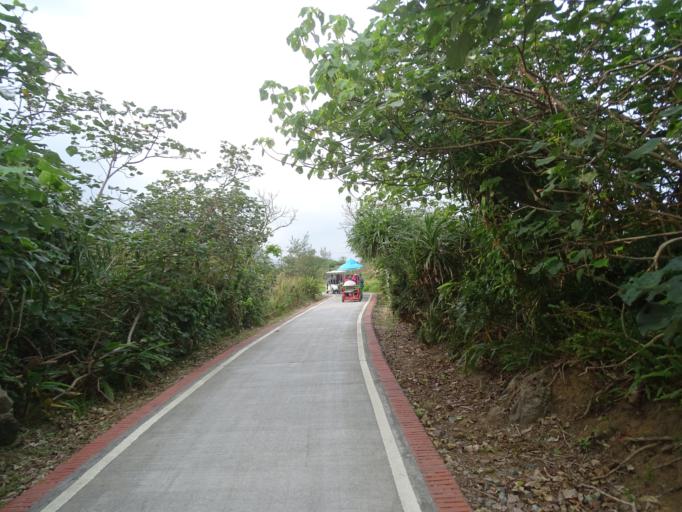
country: TW
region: Taiwan
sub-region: Keelung
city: Keelung
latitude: 25.0347
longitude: 121.9302
